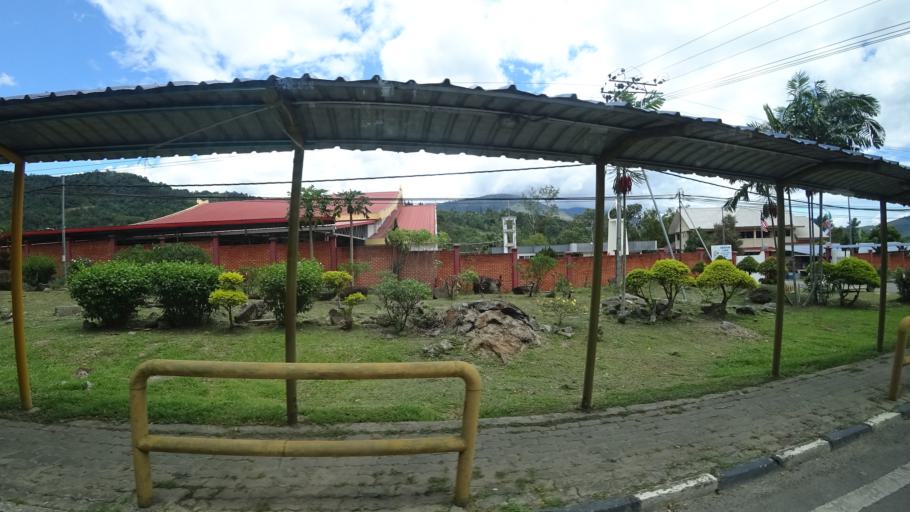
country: MY
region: Sabah
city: Ranau
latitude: 5.9543
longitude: 116.6637
